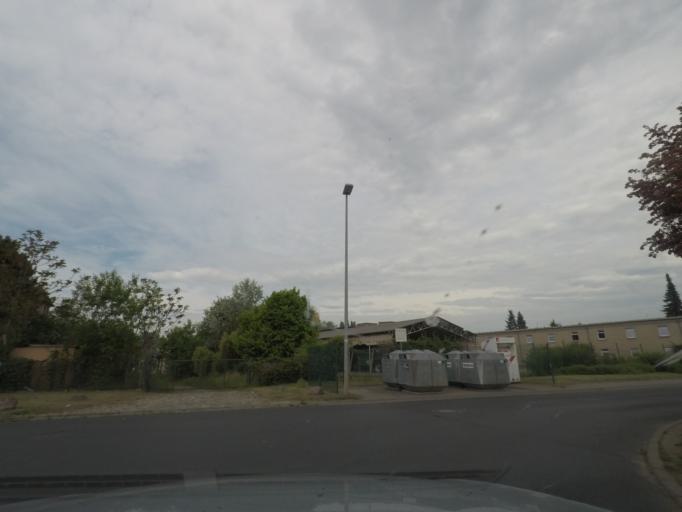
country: DE
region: Brandenburg
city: Prenzlau
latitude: 53.3257
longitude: 13.8722
